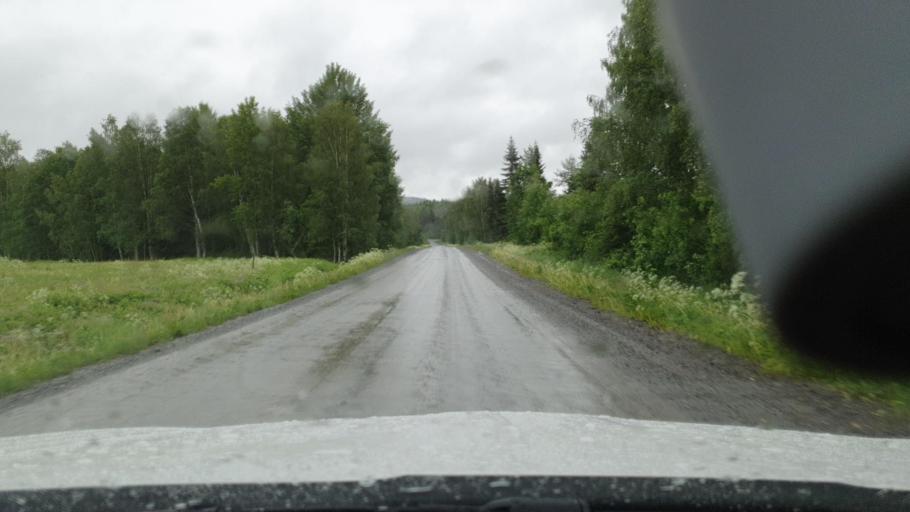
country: SE
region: Vaesterbotten
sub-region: Skelleftea Kommun
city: Burtraesk
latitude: 64.3651
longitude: 20.4050
